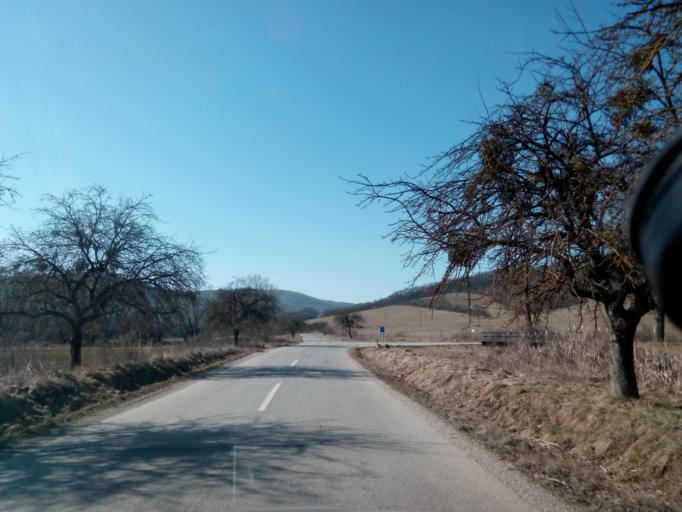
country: SK
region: Kosicky
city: Roznava
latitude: 48.5739
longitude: 20.6438
